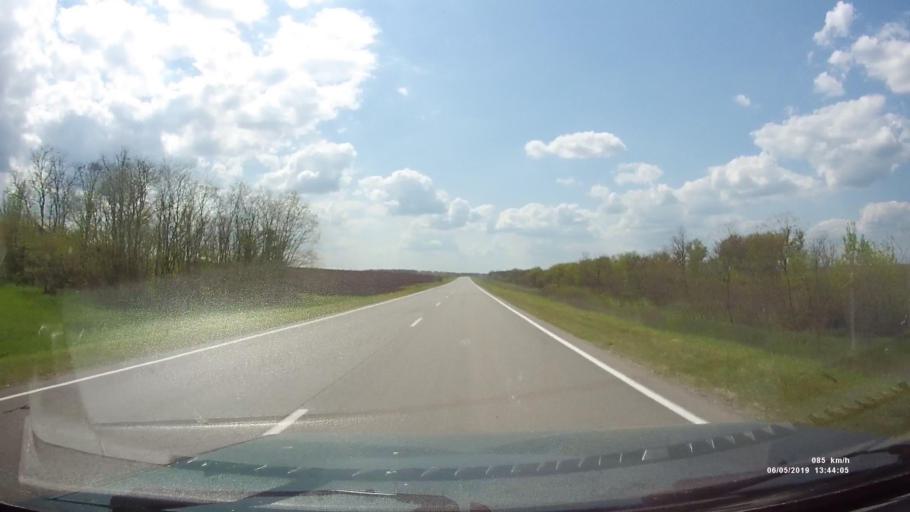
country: RU
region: Rostov
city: Melikhovskaya
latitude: 47.6597
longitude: 40.6261
